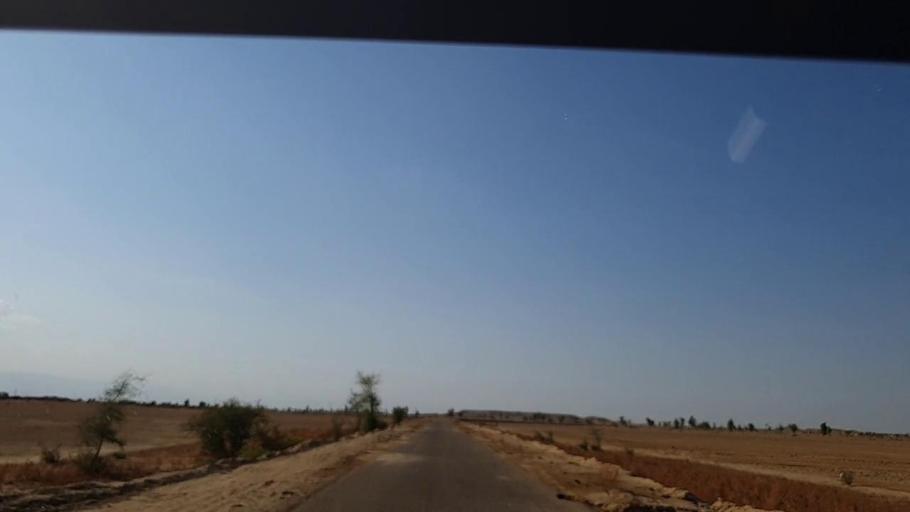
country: PK
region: Sindh
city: Johi
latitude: 26.5288
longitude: 67.5090
